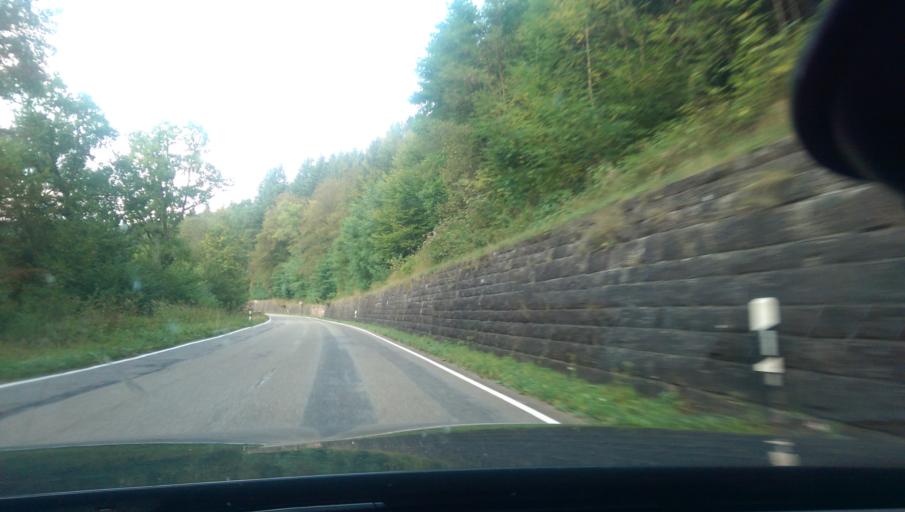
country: DE
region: Baden-Wuerttemberg
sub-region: Karlsruhe Region
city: Tiefenbronn
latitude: 48.8236
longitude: 8.7884
